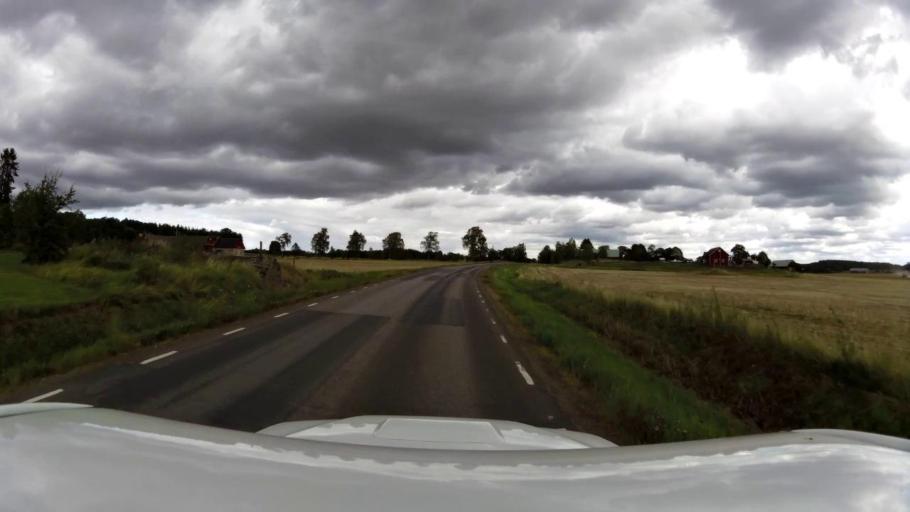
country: SE
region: OEstergoetland
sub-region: Linkopings Kommun
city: Sturefors
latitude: 58.3837
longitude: 15.7333
